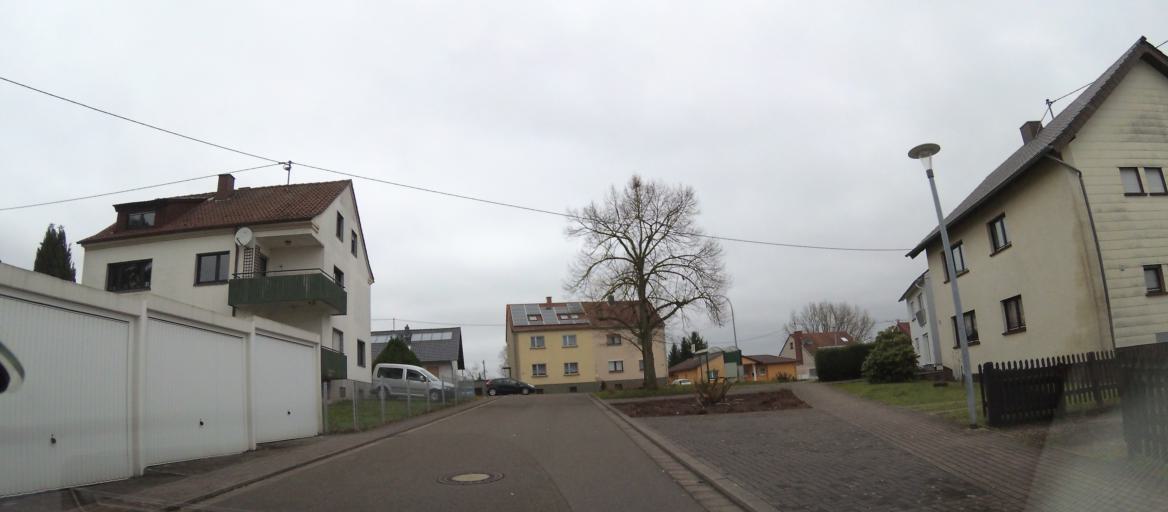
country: DE
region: Saarland
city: Schiffweiler
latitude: 49.3596
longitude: 7.1200
